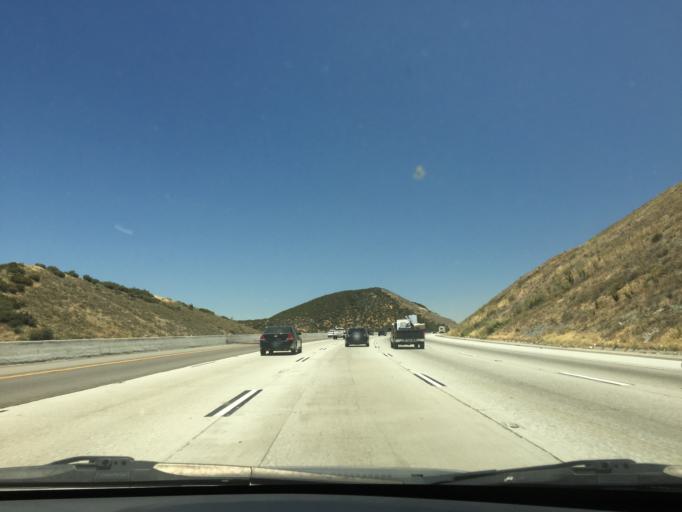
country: US
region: California
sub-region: San Bernardino County
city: Oak Hills
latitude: 34.2556
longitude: -117.4493
